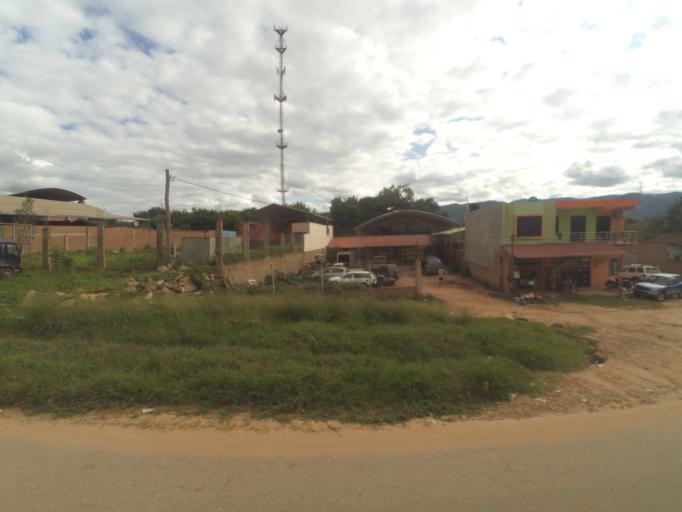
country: BO
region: Santa Cruz
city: Samaipata
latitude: -18.1642
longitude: -63.9221
